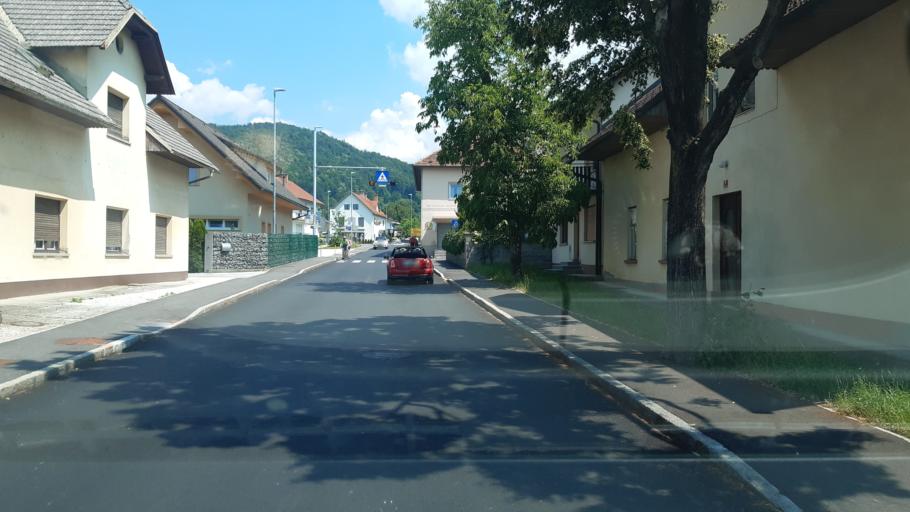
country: SI
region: Cerklje na Gorenjskem
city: Cerklje na Gorenjskem
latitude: 46.2548
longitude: 14.4876
